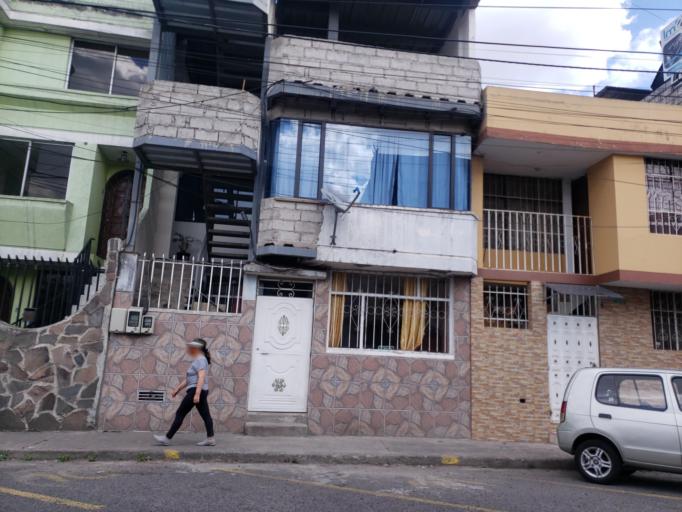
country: EC
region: Pichincha
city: Quito
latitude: -0.2719
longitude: -78.5388
